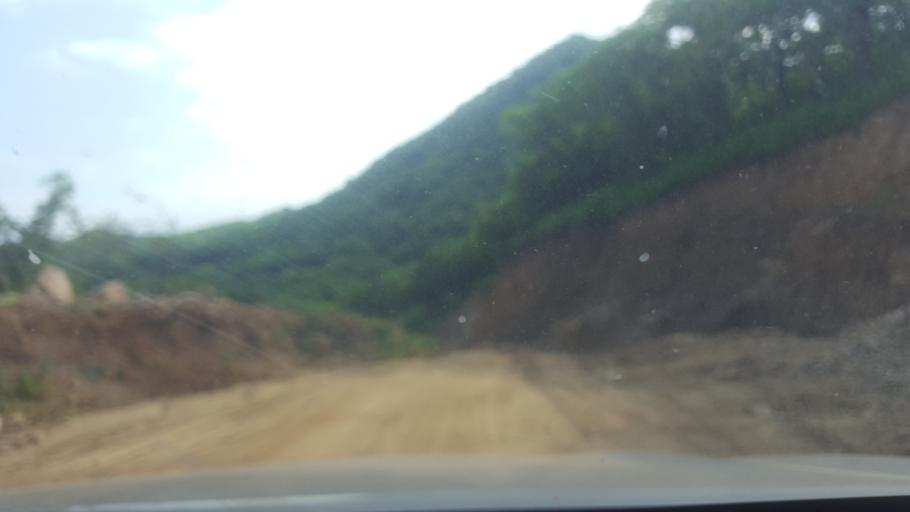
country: ET
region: Southern Nations, Nationalities, and People's Region
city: Tippi
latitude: 7.5380
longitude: 34.9726
